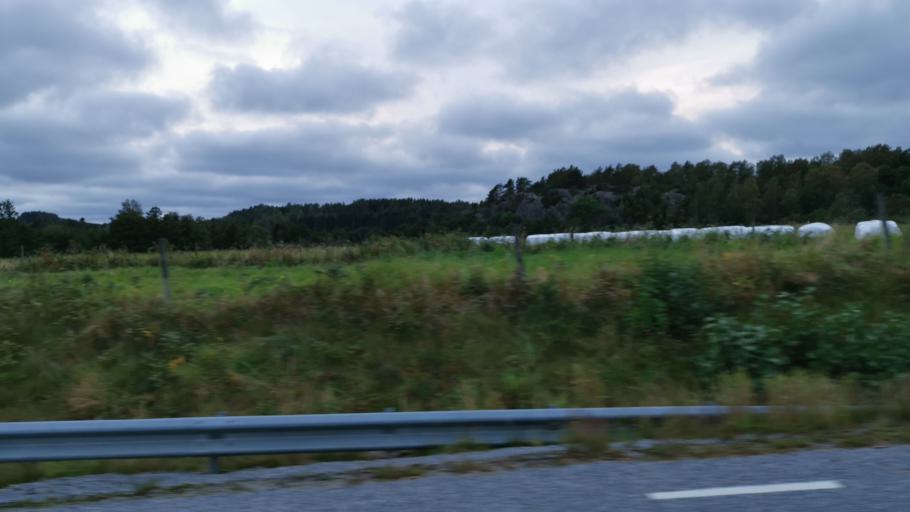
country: SE
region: Vaestra Goetaland
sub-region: Tanums Kommun
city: Tanumshede
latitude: 58.6404
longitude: 11.3406
